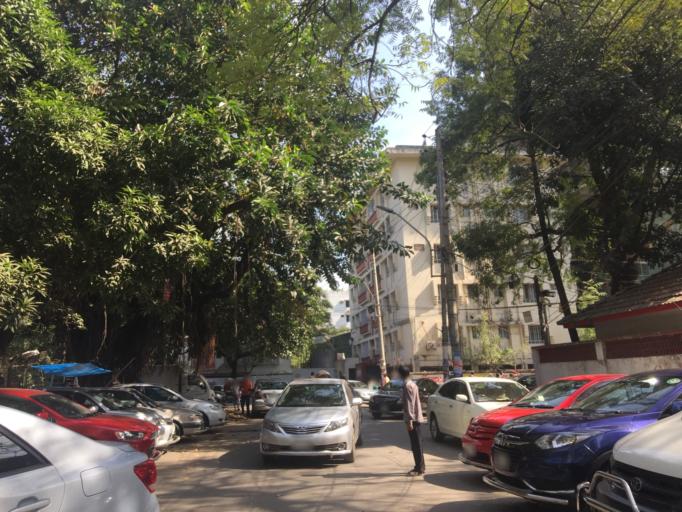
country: BD
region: Dhaka
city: Azimpur
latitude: 23.7408
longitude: 90.3803
